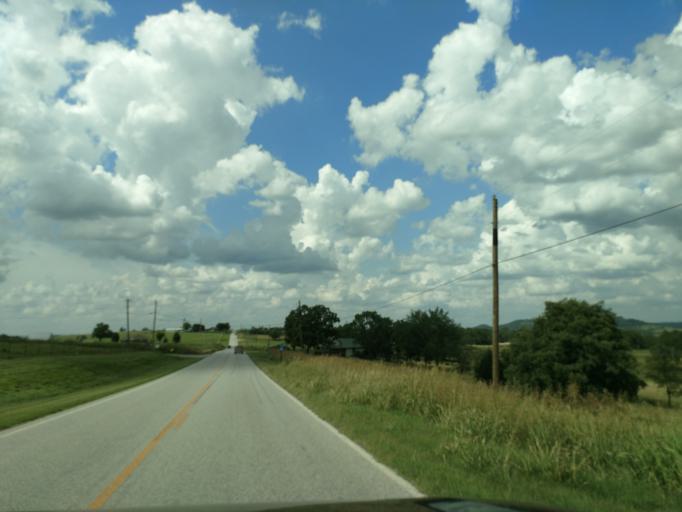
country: US
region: Arkansas
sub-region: Carroll County
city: Berryville
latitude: 36.4501
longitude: -93.5560
